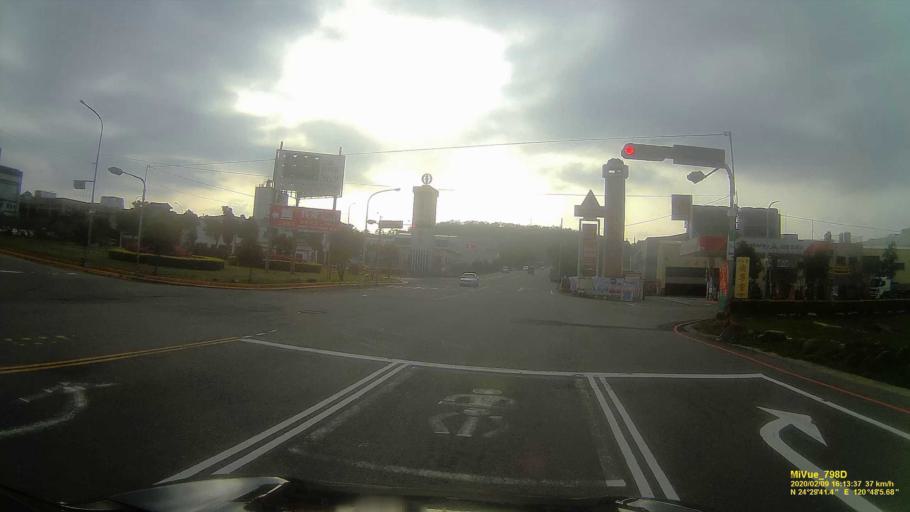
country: TW
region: Taiwan
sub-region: Miaoli
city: Miaoli
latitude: 24.4948
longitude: 120.8014
